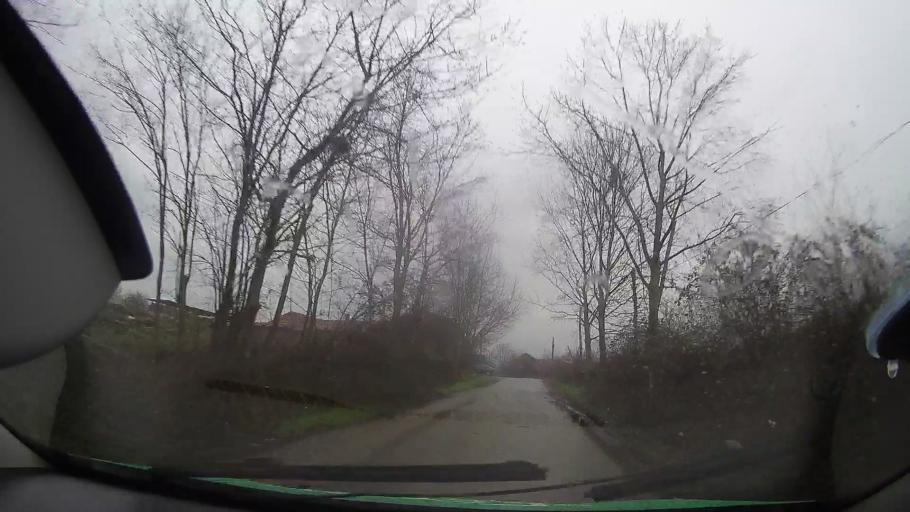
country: RO
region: Bihor
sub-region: Comuna Uileacu de Beius
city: Uileacu de Beius
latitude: 46.7047
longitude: 22.2228
